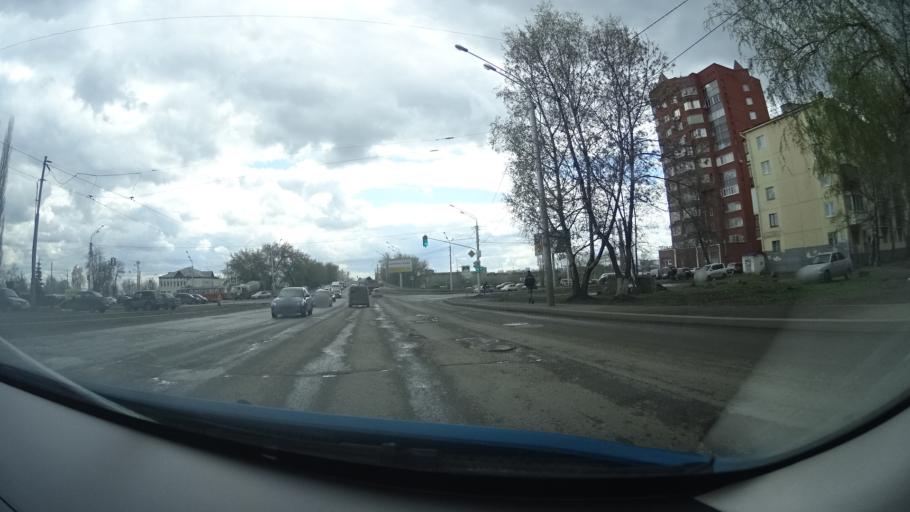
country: RU
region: Bashkortostan
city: Ufa
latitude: 54.8113
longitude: 56.0879
